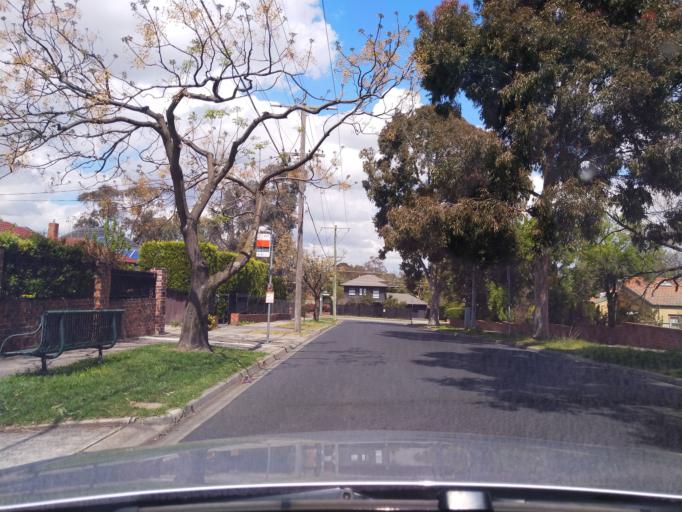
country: AU
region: Victoria
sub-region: Banyule
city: Bellfield
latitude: -37.7568
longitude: 145.0496
